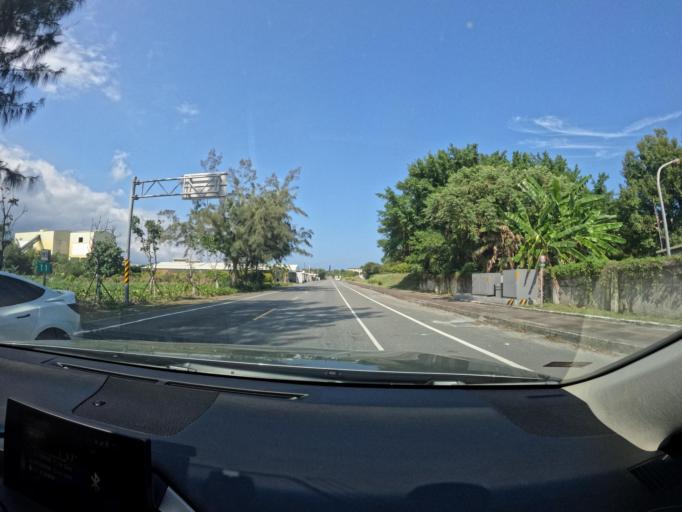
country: TW
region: Taiwan
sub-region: Hualien
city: Hualian
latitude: 24.0116
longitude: 121.6339
